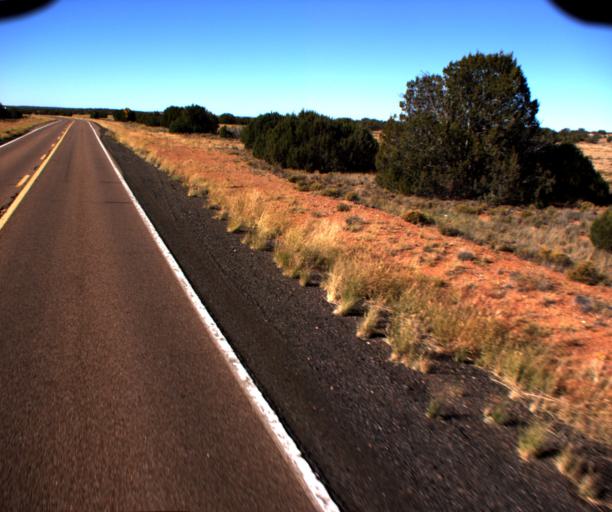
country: US
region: Arizona
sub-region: Navajo County
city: Heber-Overgaard
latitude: 34.5734
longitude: -110.4116
